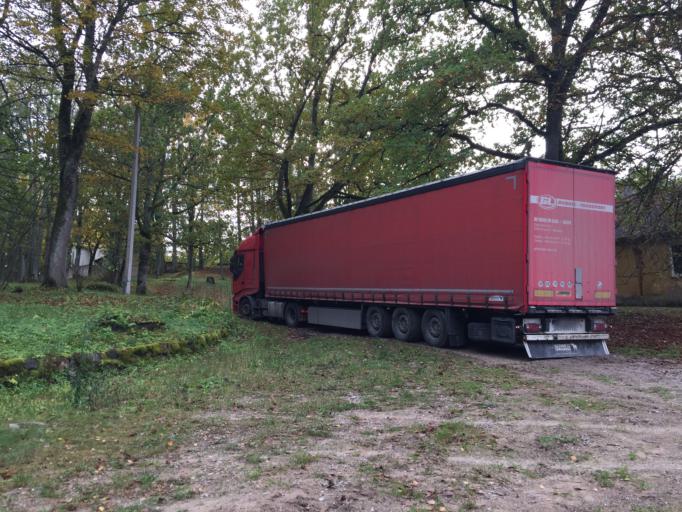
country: LV
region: Auces Novads
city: Auce
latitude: 56.5505
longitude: 23.0185
